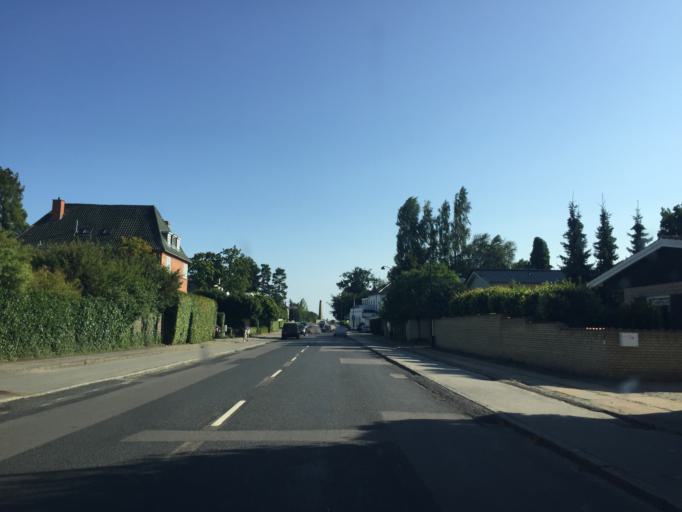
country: DK
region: Capital Region
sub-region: Gentofte Kommune
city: Charlottenlund
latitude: 55.7600
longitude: 12.5584
